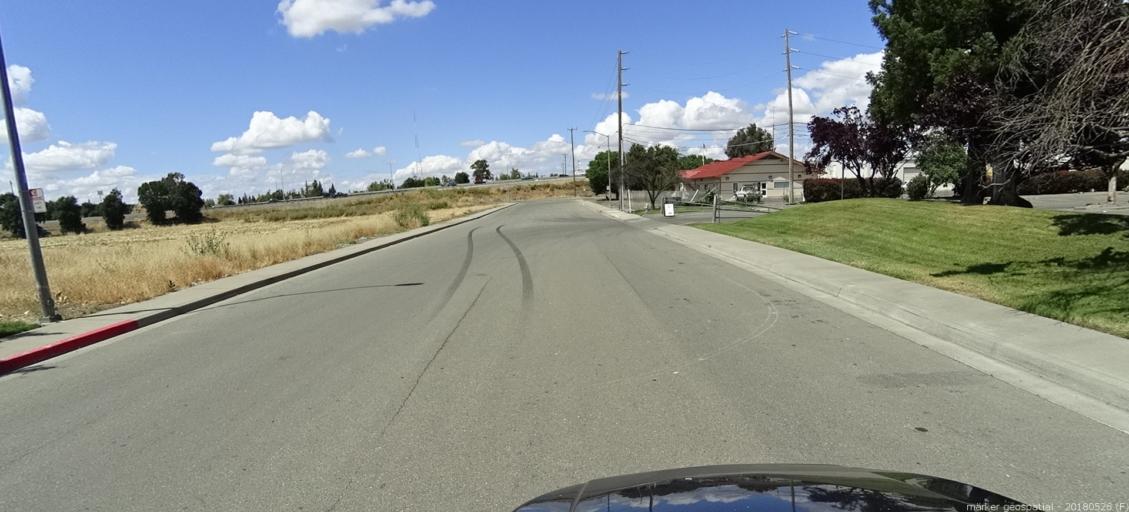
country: US
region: California
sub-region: Sacramento County
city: Rio Linda
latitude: 38.6389
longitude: -121.4755
